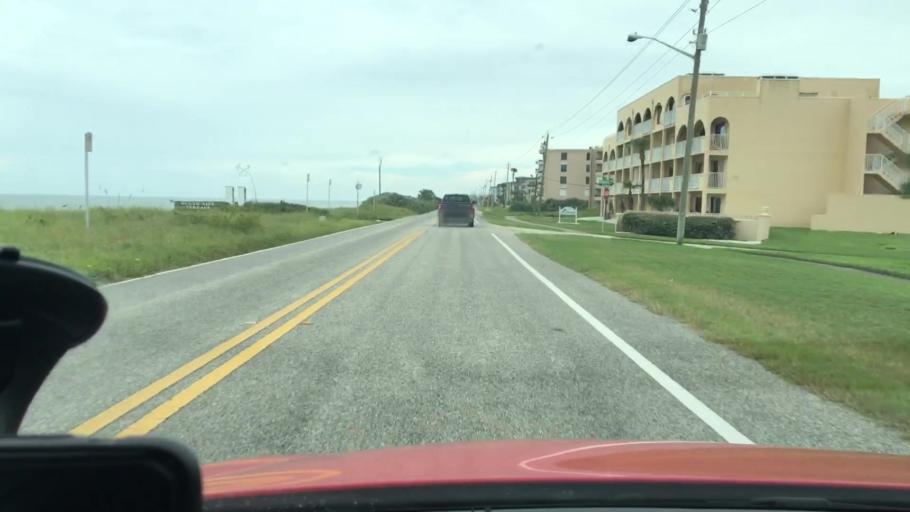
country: US
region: Florida
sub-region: Volusia County
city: Ormond-by-the-Sea
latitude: 29.3769
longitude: -81.0797
